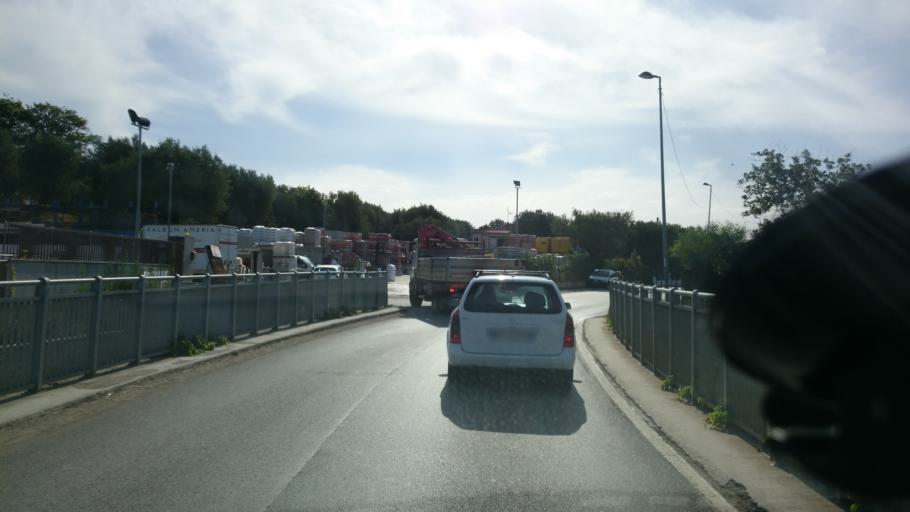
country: IT
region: Campania
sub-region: Provincia di Salerno
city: Marina di Camerota
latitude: 40.0031
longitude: 15.3658
